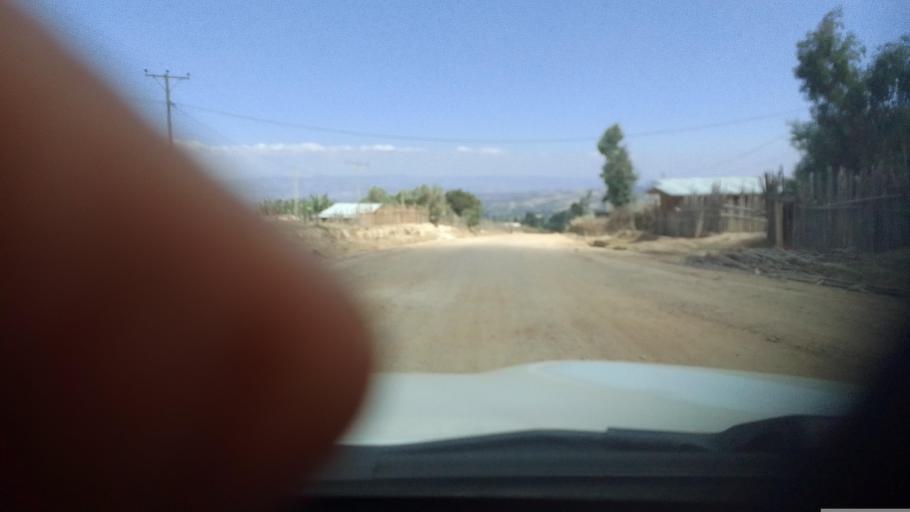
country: ET
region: Oromiya
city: Hagere Hiywet
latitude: 8.8465
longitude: 37.8868
